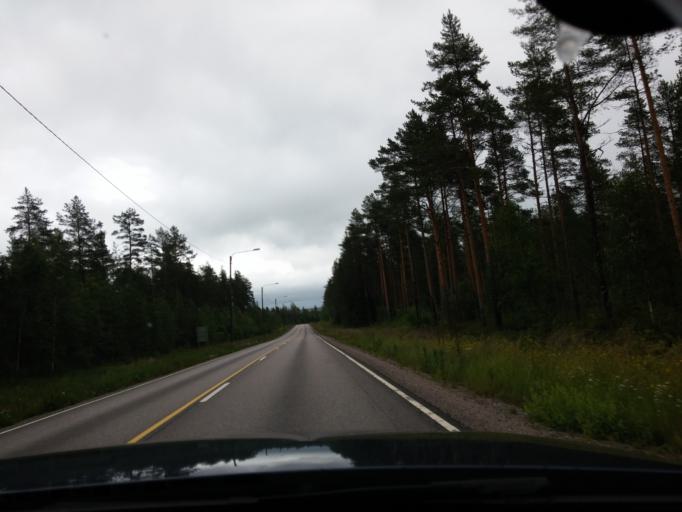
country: FI
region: Central Finland
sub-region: Saarijaervi-Viitasaari
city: Pylkoenmaeki
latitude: 62.6389
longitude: 24.8291
